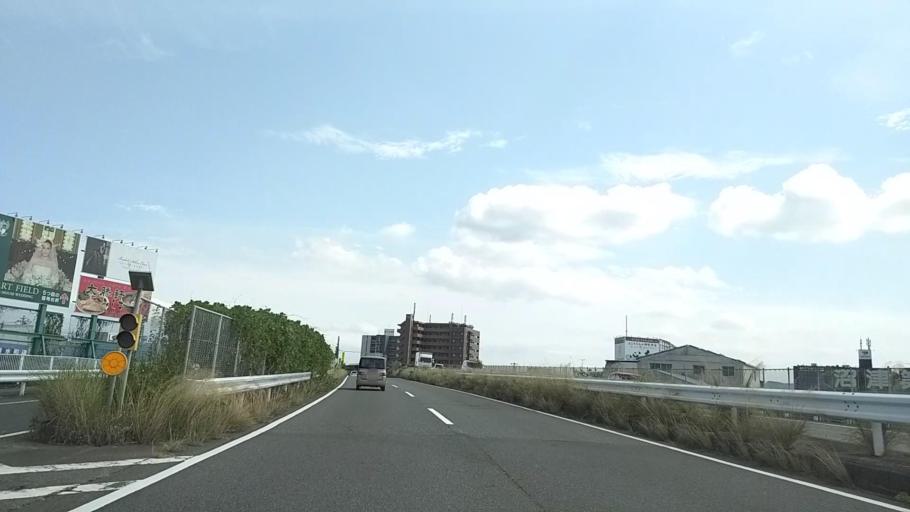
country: JP
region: Shizuoka
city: Mishima
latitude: 35.1116
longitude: 138.8926
